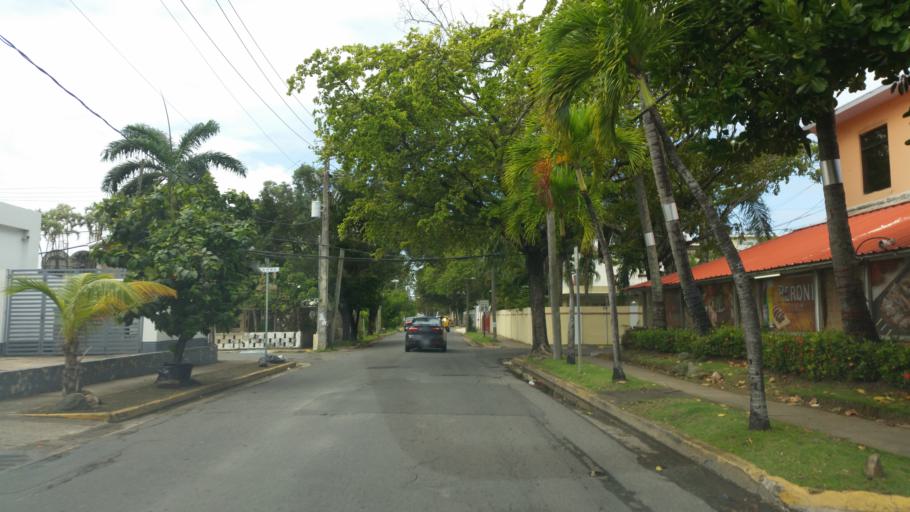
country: PR
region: San Juan
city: San Juan
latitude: 18.4518
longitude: -66.0403
